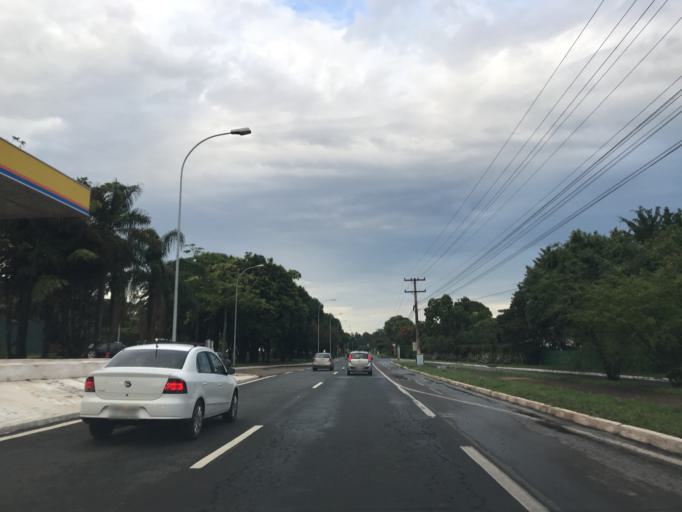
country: BR
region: Federal District
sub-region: Brasilia
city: Brasilia
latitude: -15.8437
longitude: -47.8709
